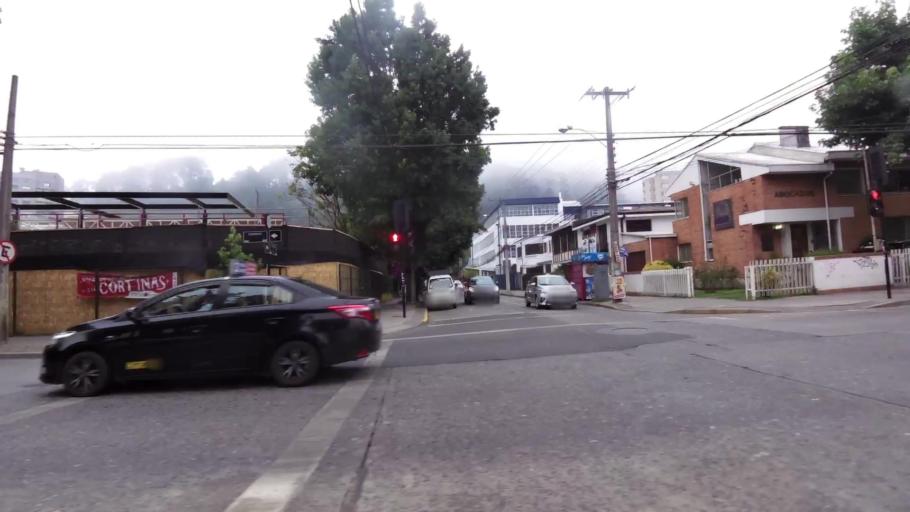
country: CL
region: Biobio
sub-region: Provincia de Concepcion
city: Concepcion
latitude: -36.8298
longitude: -73.0462
